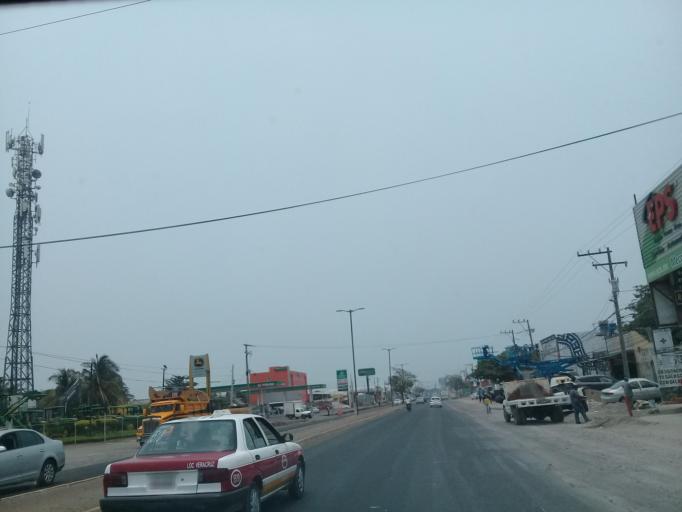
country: MX
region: Veracruz
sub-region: Veracruz
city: Las Amapolas
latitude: 19.1610
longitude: -96.2038
